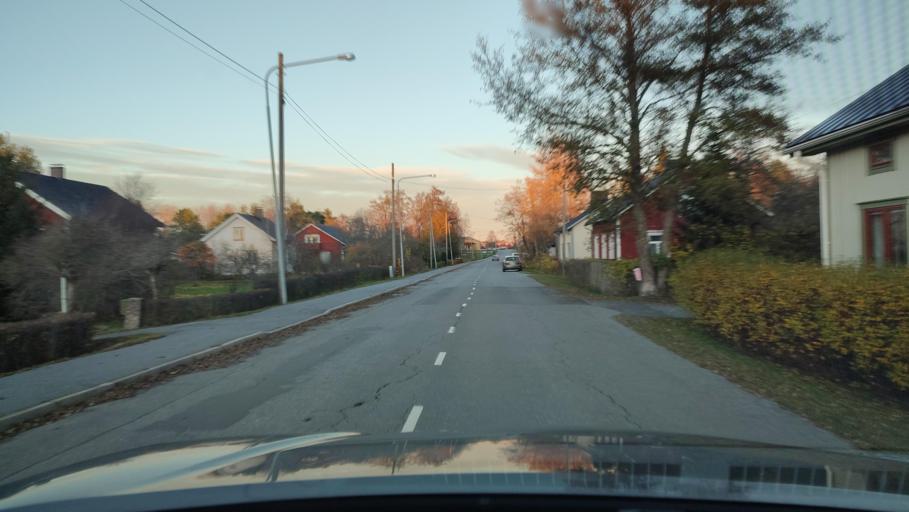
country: FI
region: Ostrobothnia
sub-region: Sydosterbotten
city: Kristinestad
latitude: 62.2661
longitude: 21.3663
